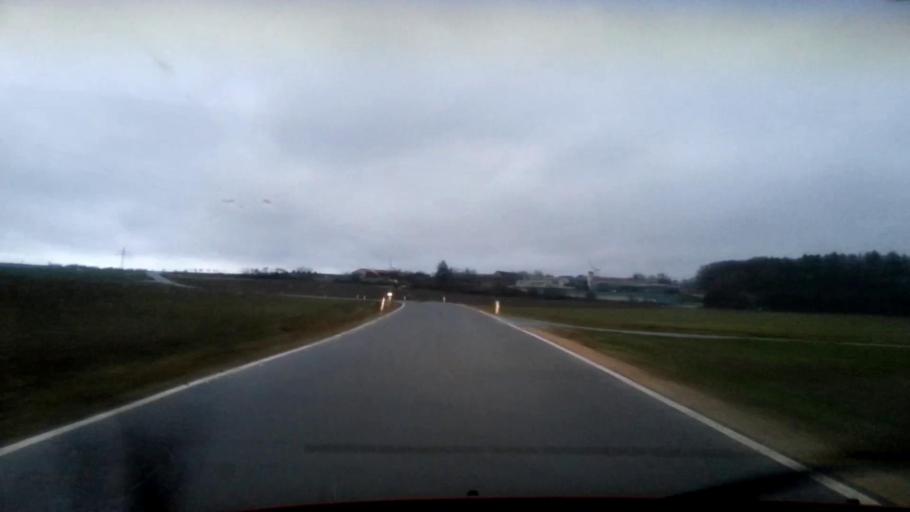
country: DE
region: Bavaria
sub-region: Upper Franconia
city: Poxdorf
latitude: 49.9660
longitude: 11.1353
